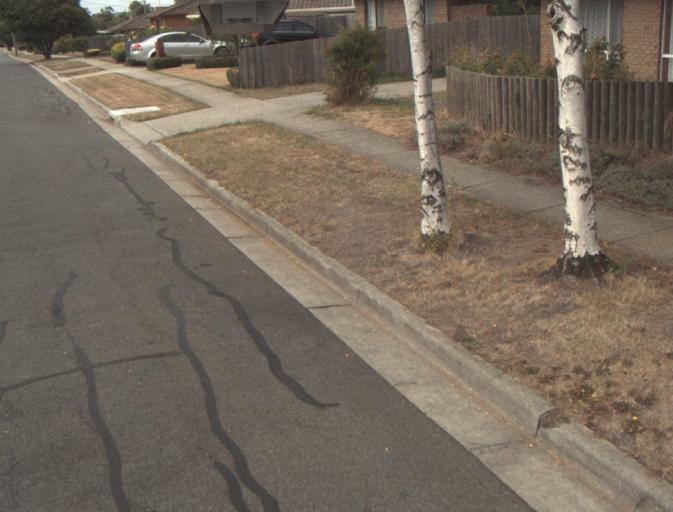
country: AU
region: Tasmania
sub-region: Launceston
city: Invermay
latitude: -41.3907
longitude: 147.1186
